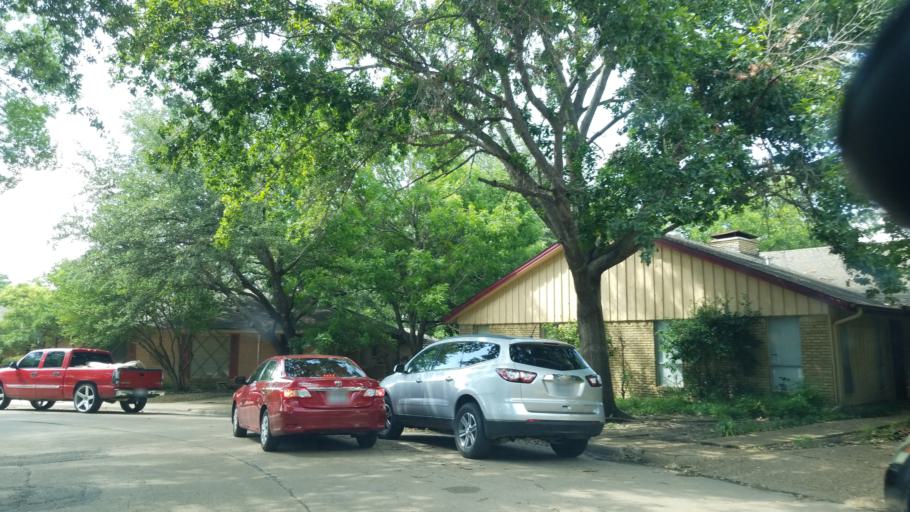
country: US
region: Texas
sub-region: Dallas County
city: Farmers Branch
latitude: 32.8827
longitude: -96.8582
